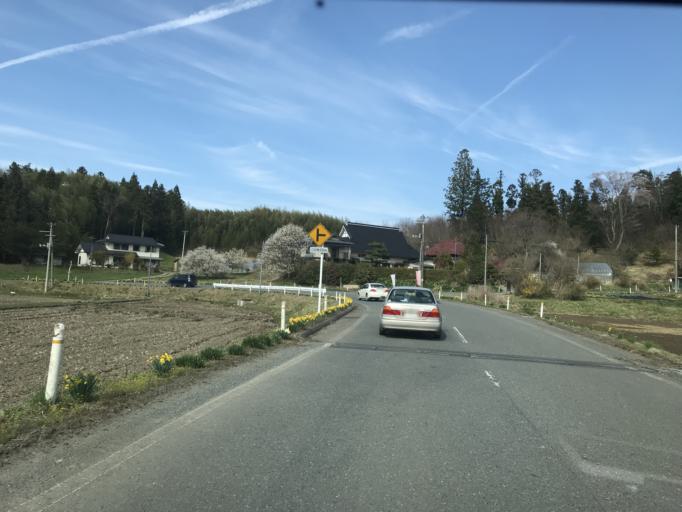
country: JP
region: Iwate
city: Ichinoseki
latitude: 38.8964
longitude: 141.3875
